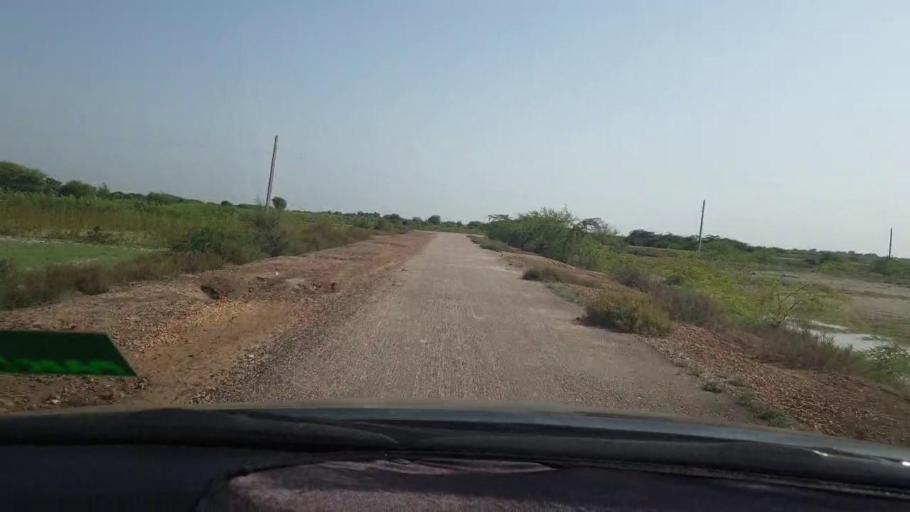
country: PK
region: Sindh
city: Naukot
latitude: 24.9425
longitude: 69.2461
